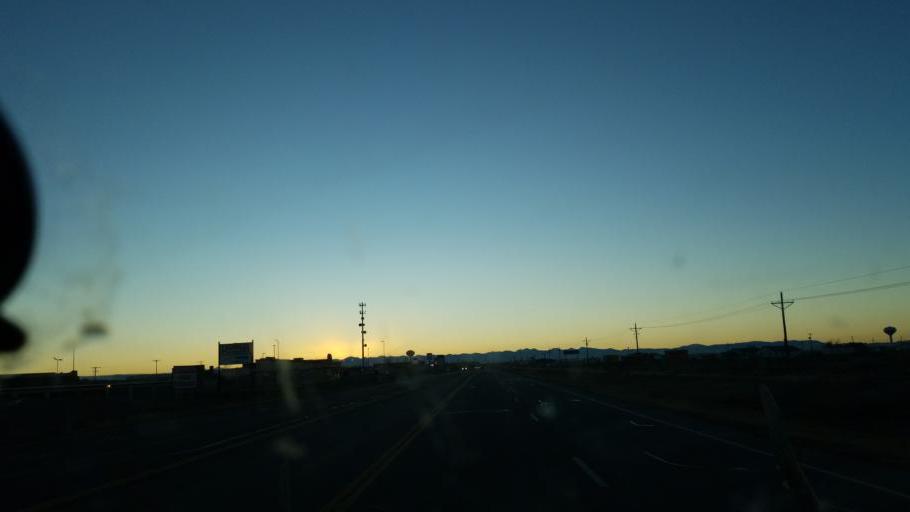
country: US
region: Colorado
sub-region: Alamosa County
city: Alamosa
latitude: 37.4793
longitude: -105.9047
